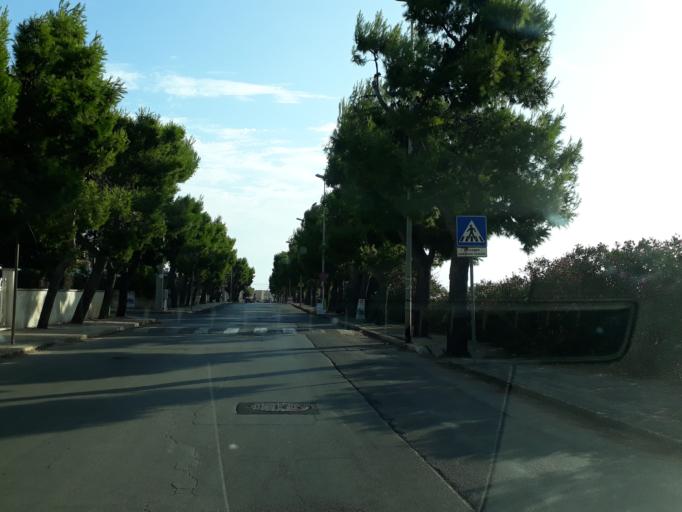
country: IT
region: Apulia
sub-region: Provincia di Brindisi
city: Carovigno
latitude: 40.7543
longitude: 17.6993
